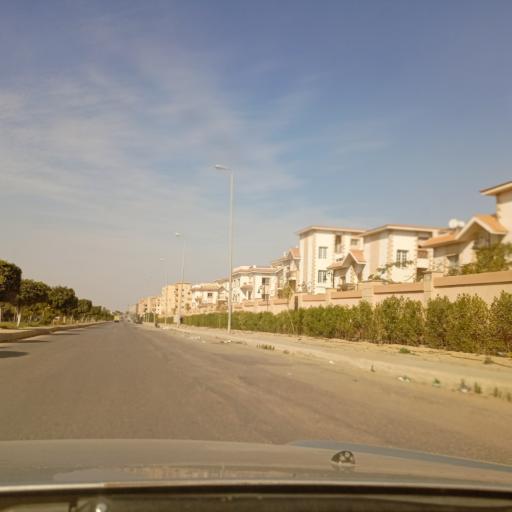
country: EG
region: Muhafazat al Qalyubiyah
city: Al Khankah
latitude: 30.0395
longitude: 31.4852
